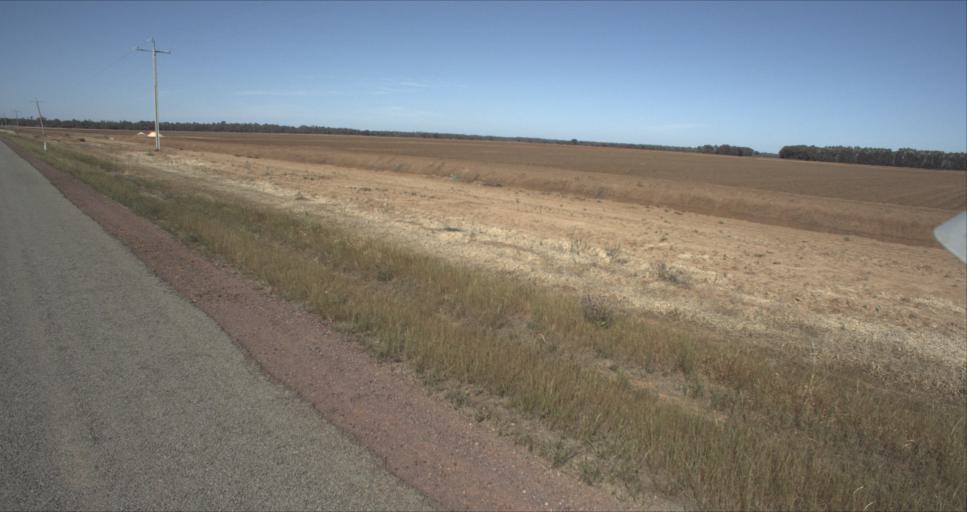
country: AU
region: New South Wales
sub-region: Leeton
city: Leeton
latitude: -34.5927
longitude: 146.2593
